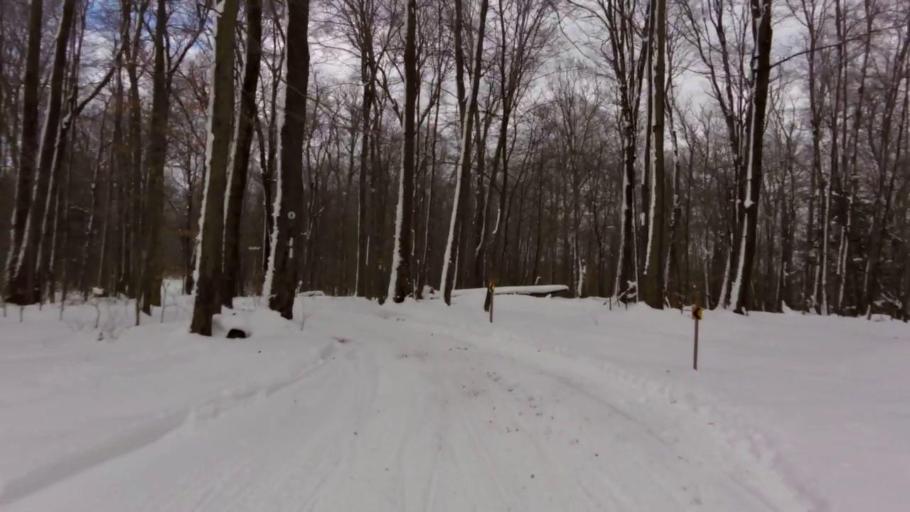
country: US
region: New York
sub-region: Cattaraugus County
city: Salamanca
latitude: 42.0453
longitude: -78.7570
